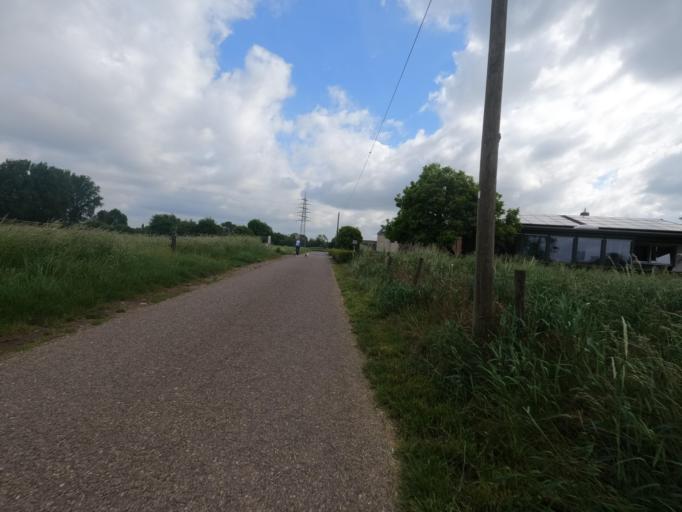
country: DE
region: North Rhine-Westphalia
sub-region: Regierungsbezirk Koln
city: Wassenberg
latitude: 51.0663
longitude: 6.1517
